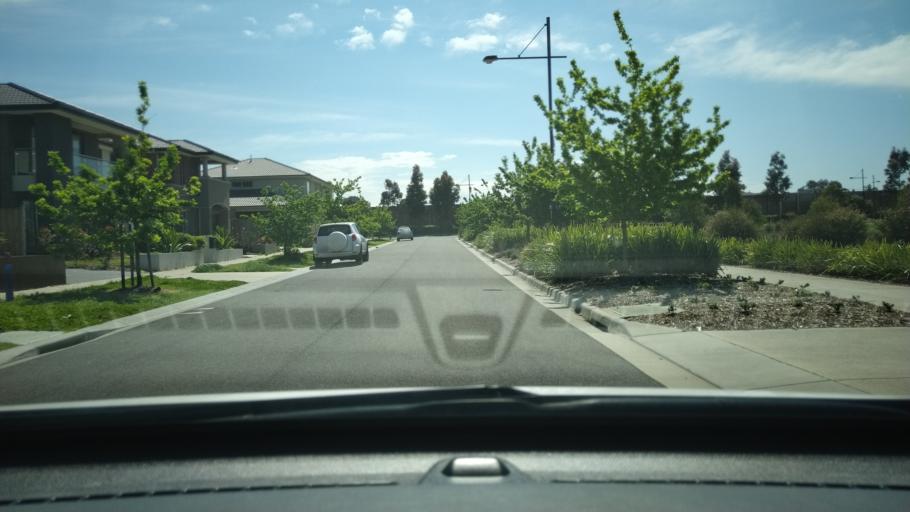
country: AU
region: Victoria
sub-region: Greater Dandenong
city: Keysborough
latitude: -37.9989
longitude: 145.1645
